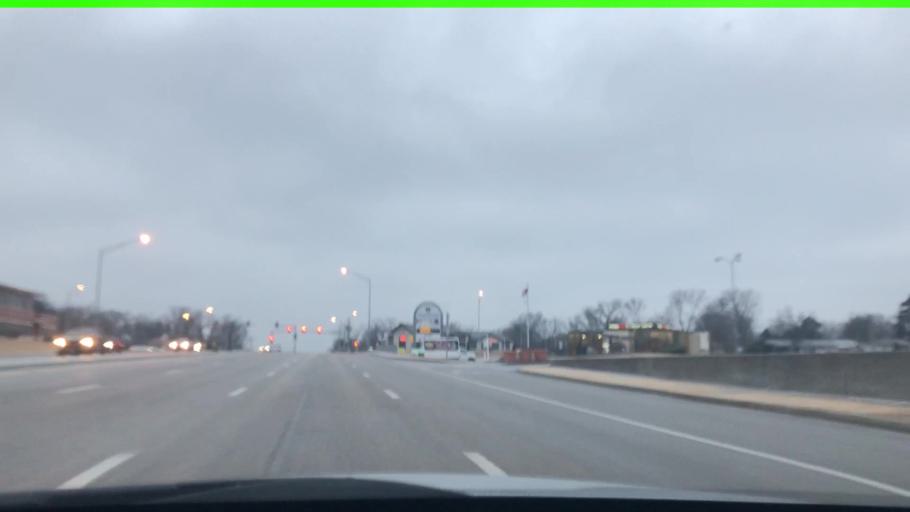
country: US
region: Missouri
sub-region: Boone County
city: Columbia
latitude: 38.9555
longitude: -92.3718
